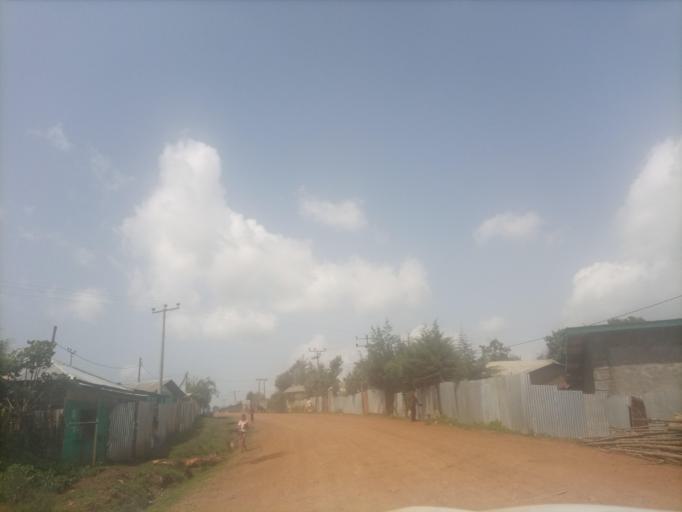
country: ET
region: Oromiya
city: Agaro
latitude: 7.7866
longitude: 36.4198
